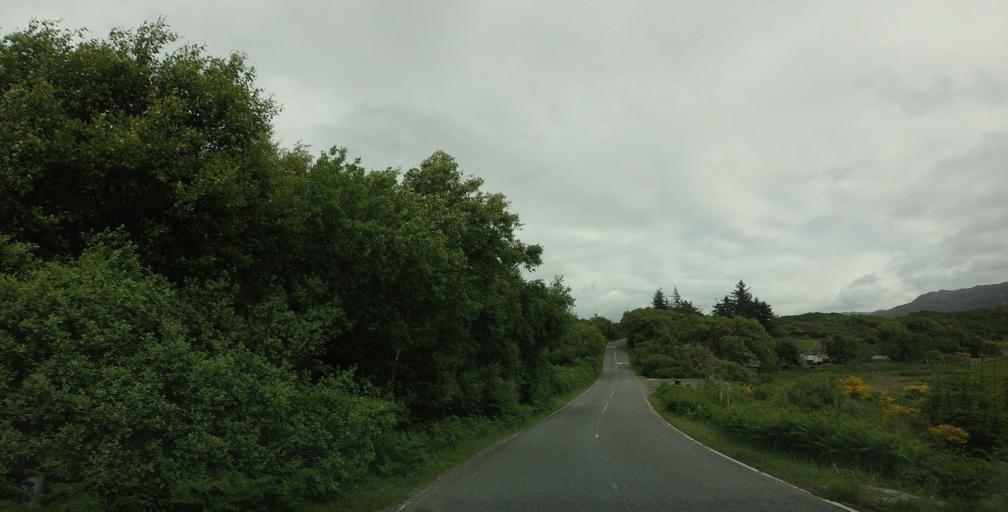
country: GB
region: Scotland
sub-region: Argyll and Bute
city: Isle Of Mull
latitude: 56.9594
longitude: -5.8412
